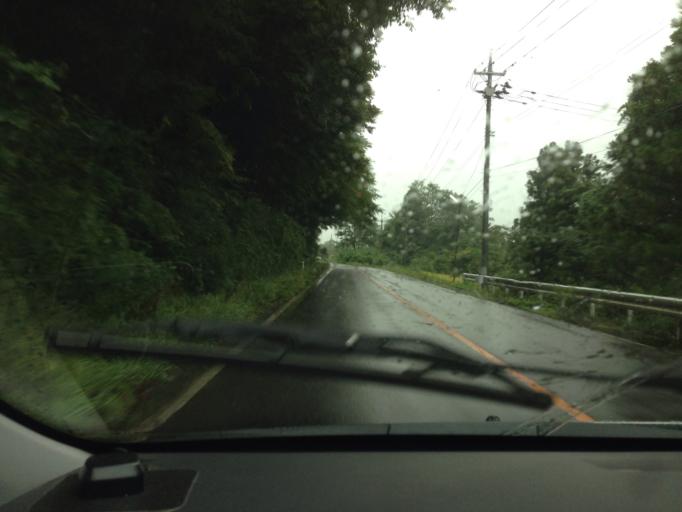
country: JP
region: Fukushima
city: Koriyama
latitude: 37.4148
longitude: 140.2945
